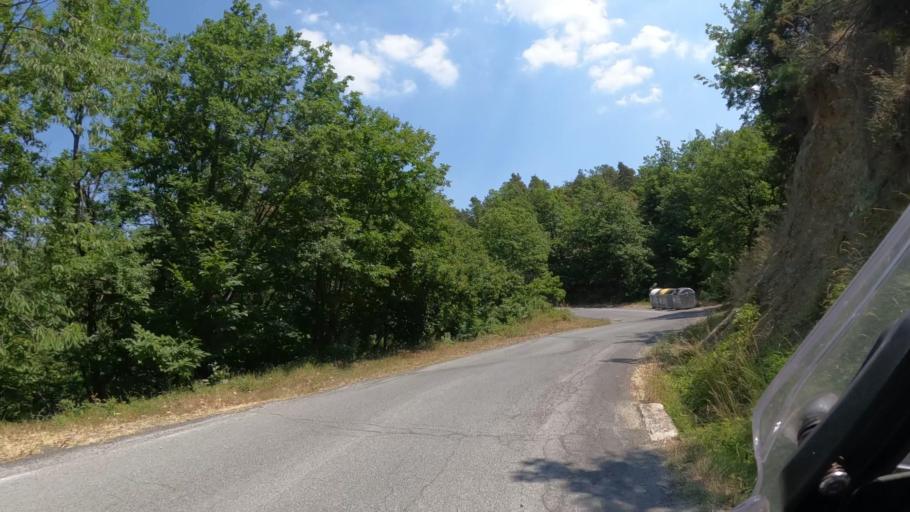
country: IT
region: Piedmont
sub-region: Provincia di Alessandria
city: Morbello
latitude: 44.5572
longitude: 8.5097
